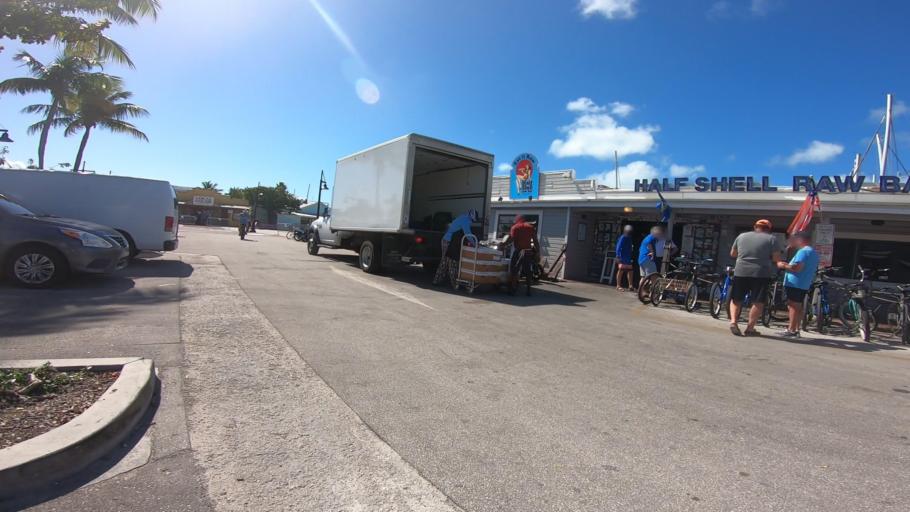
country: US
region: Florida
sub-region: Monroe County
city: Key West
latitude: 24.5618
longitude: -81.8000
